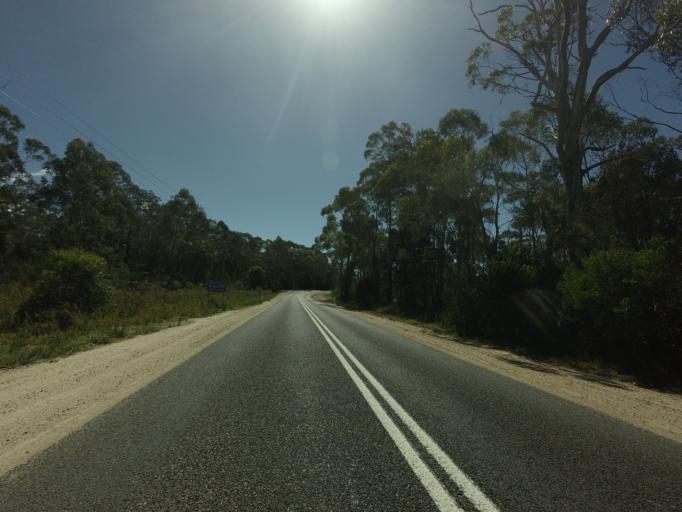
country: AU
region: Tasmania
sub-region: Break O'Day
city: St Helens
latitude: -41.8405
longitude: 148.2542
